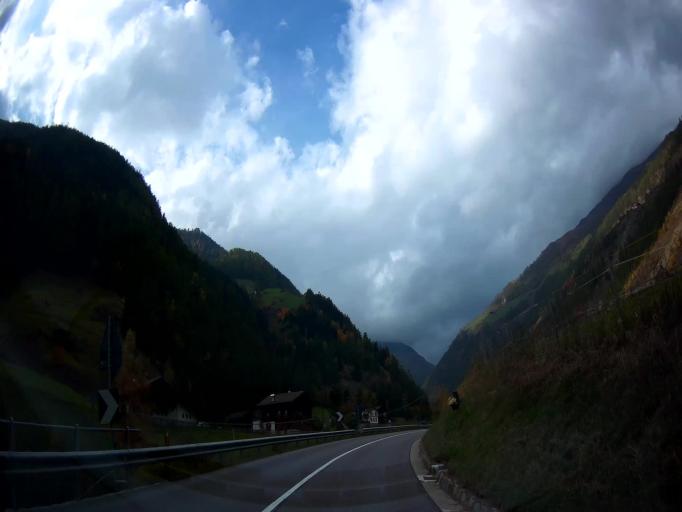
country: IT
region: Trentino-Alto Adige
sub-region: Bolzano
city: Senales
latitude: 46.7086
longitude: 10.9052
